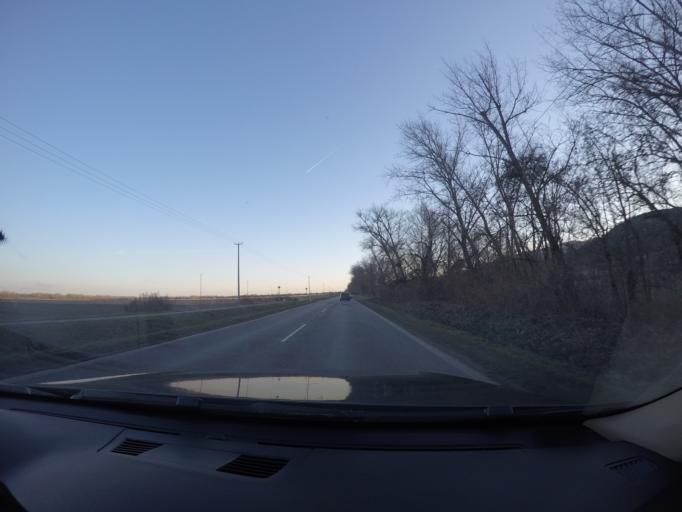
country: HU
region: Pest
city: Dunabogdany
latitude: 47.7845
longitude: 19.0463
